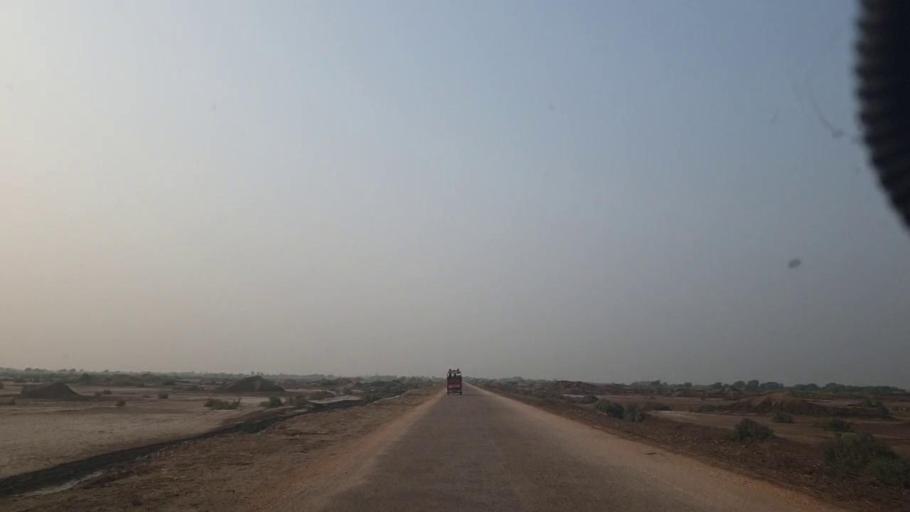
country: PK
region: Sindh
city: Bulri
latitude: 24.8540
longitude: 68.4036
